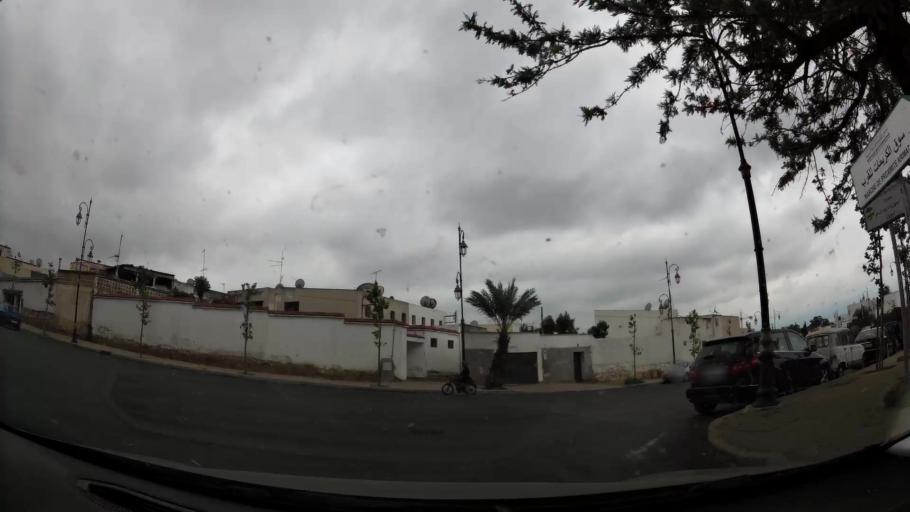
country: MA
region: Rabat-Sale-Zemmour-Zaer
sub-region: Rabat
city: Rabat
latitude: 33.9982
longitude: -6.8202
